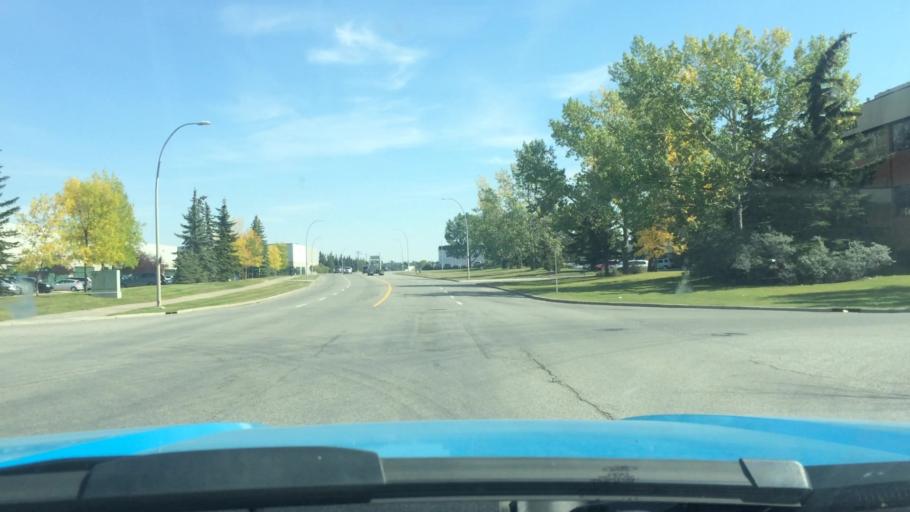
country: CA
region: Alberta
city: Calgary
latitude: 51.0886
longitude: -113.9981
